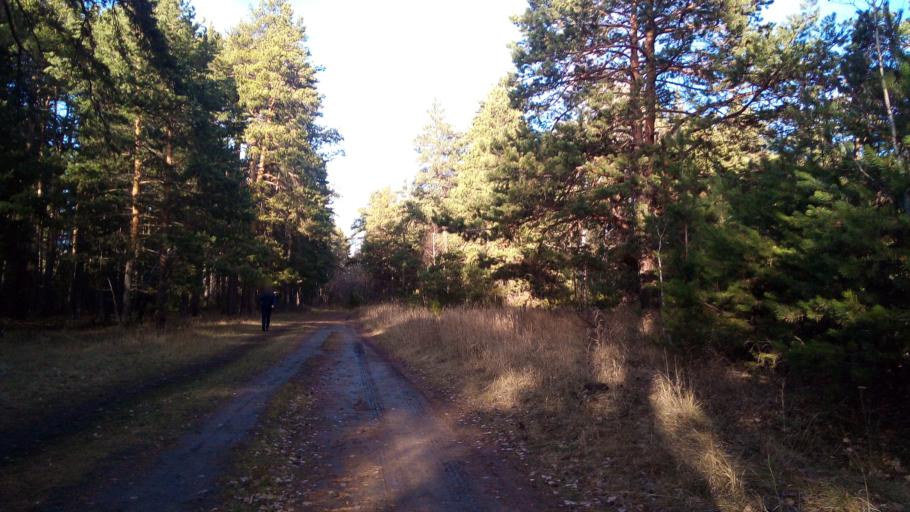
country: RU
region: Chelyabinsk
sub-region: Gorod Chelyabinsk
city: Chelyabinsk
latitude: 55.1565
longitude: 61.3522
